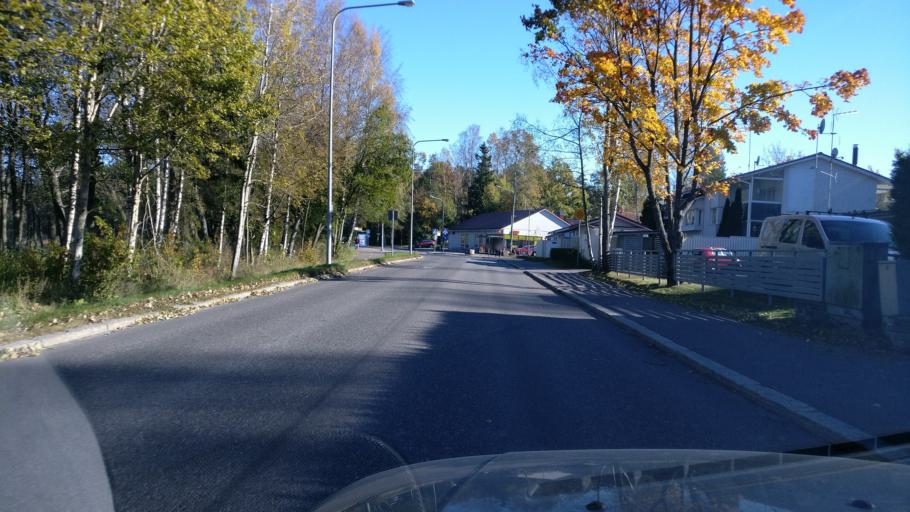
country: FI
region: Uusimaa
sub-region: Helsinki
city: Helsinki
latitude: 60.1649
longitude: 25.0598
